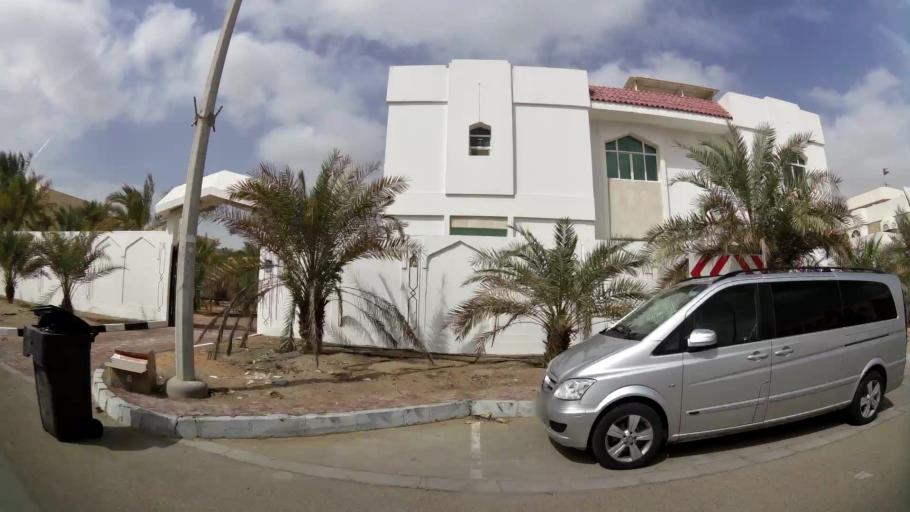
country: AE
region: Abu Dhabi
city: Abu Dhabi
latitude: 24.4013
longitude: 54.5145
